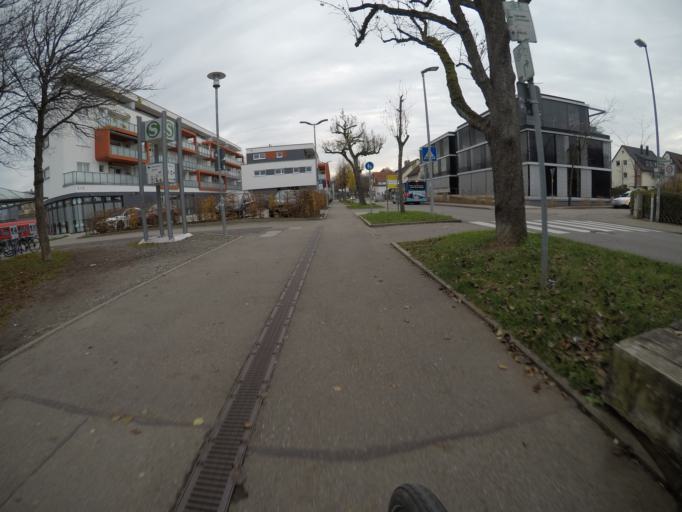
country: DE
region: Baden-Wuerttemberg
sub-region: Regierungsbezirk Stuttgart
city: Leinfelden-Echterdingen
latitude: 48.6954
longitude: 9.1426
